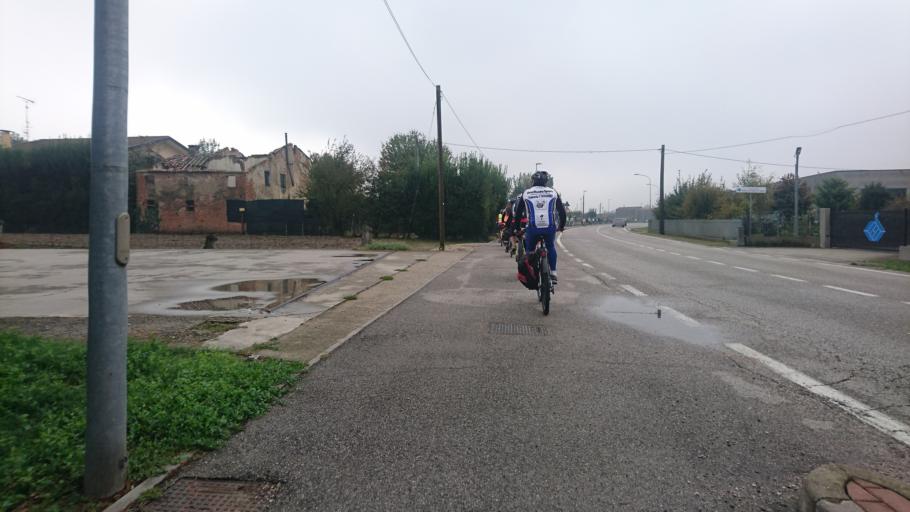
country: IT
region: Veneto
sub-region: Provincia di Padova
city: Pozzonovo
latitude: 45.2060
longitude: 11.7821
